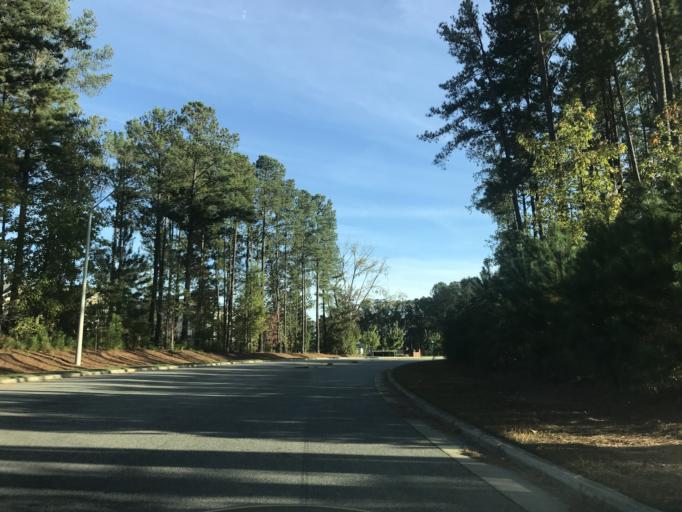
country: US
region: North Carolina
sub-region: Wake County
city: Wake Forest
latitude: 35.8933
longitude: -78.5555
